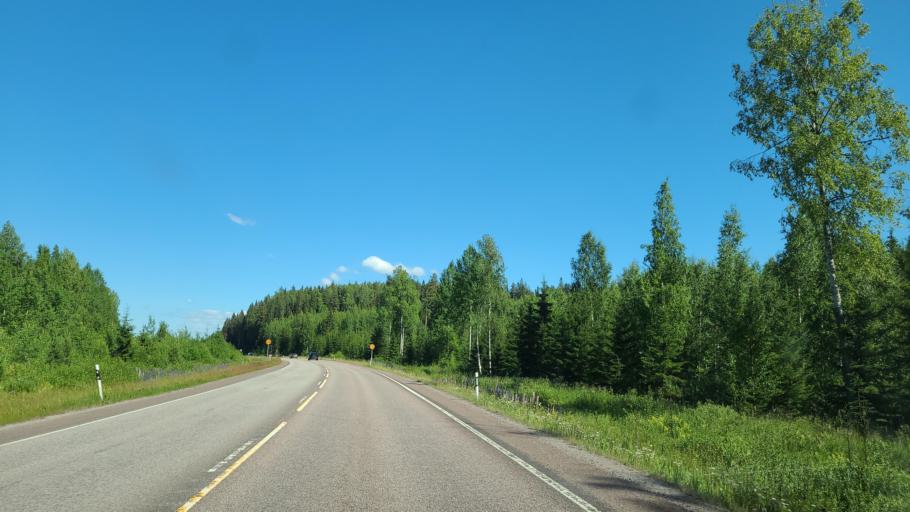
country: FI
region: Central Finland
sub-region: Jyvaeskylae
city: Petaejaevesi
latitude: 62.2716
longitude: 25.3736
